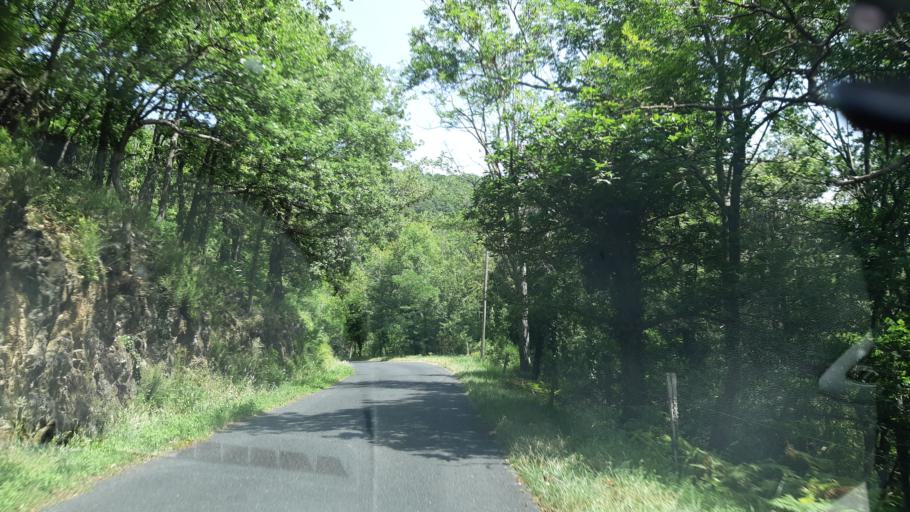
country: FR
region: Languedoc-Roussillon
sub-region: Departement des Pyrenees-Orientales
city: Arles
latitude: 42.5300
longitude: 2.6115
